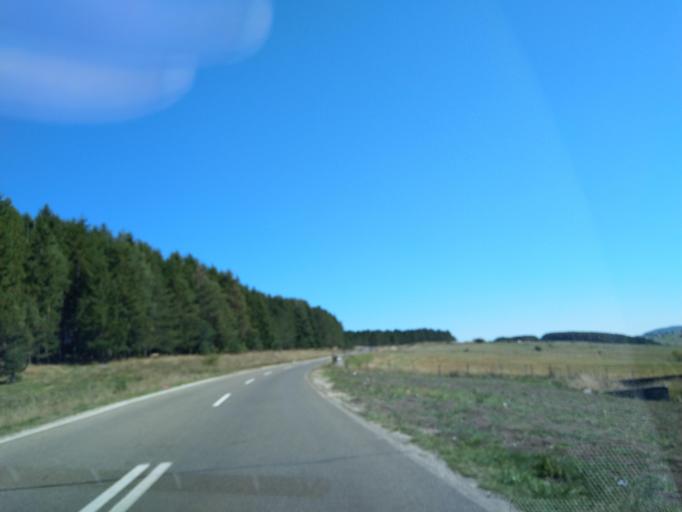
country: RS
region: Central Serbia
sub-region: Zlatiborski Okrug
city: Sjenica
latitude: 43.2681
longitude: 20.0303
